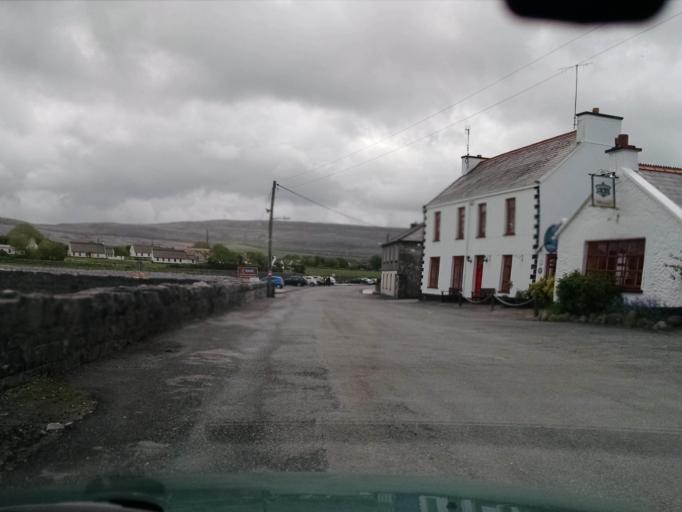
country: IE
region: Connaught
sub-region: County Galway
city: Bearna
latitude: 53.1201
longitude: -9.1545
